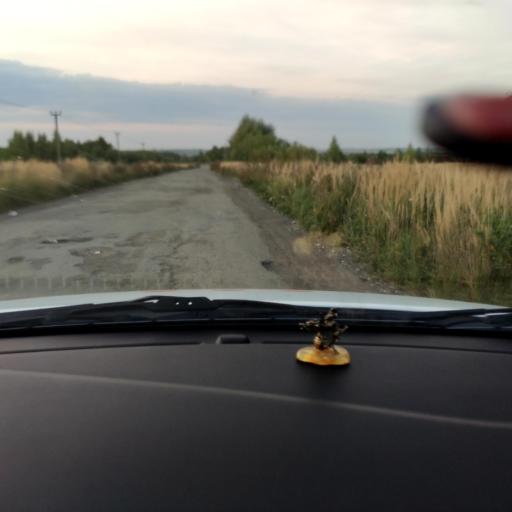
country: RU
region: Tatarstan
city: Vysokaya Gora
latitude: 55.8091
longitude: 49.3134
